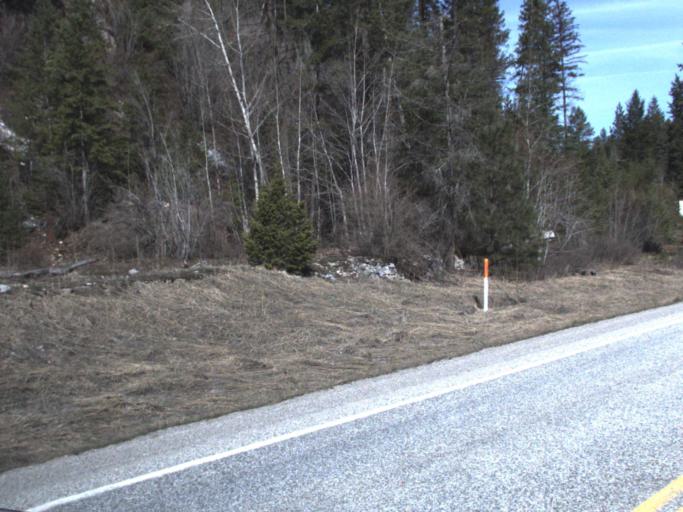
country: US
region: Washington
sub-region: Stevens County
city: Colville
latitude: 48.5332
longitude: -117.8221
